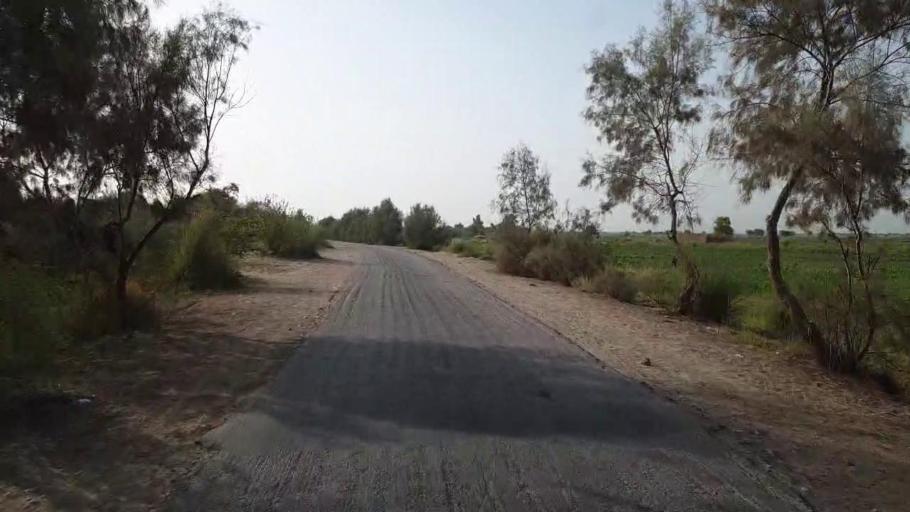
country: PK
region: Sindh
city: Jam Sahib
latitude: 26.4890
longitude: 68.8599
